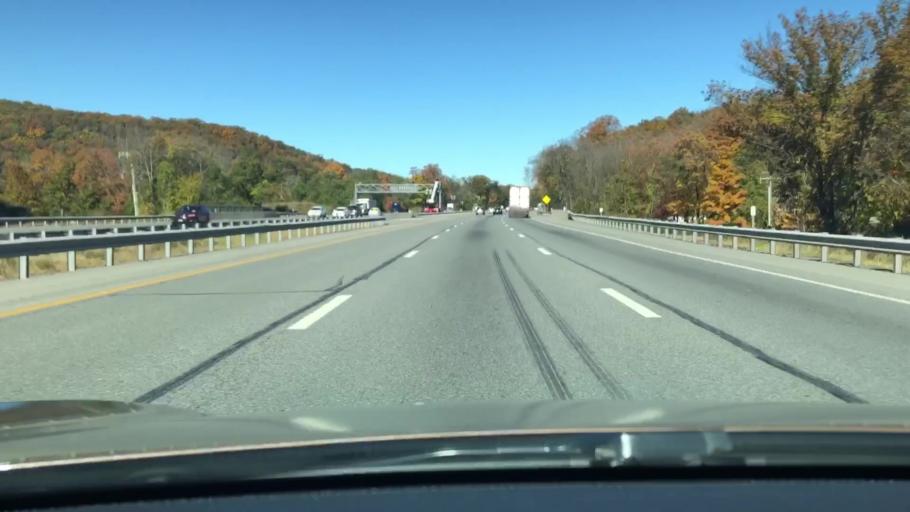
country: US
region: New York
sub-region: Rockland County
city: Sloatsburg
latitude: 41.1923
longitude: -74.1816
